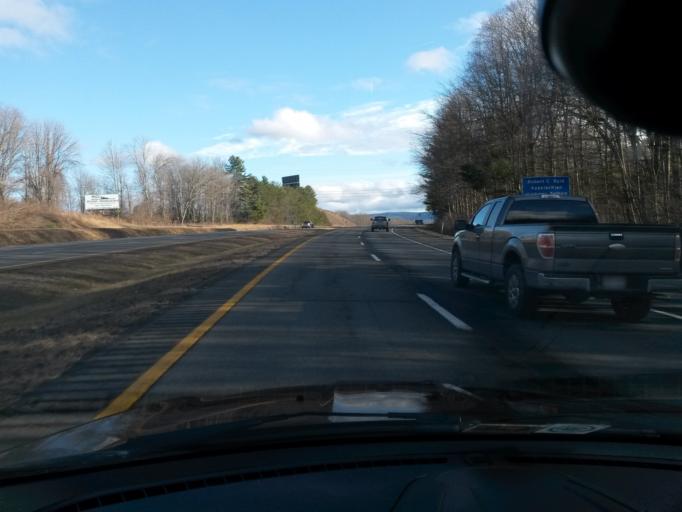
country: US
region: West Virginia
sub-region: Mercer County
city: Athens
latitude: 37.3638
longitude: -81.0326
